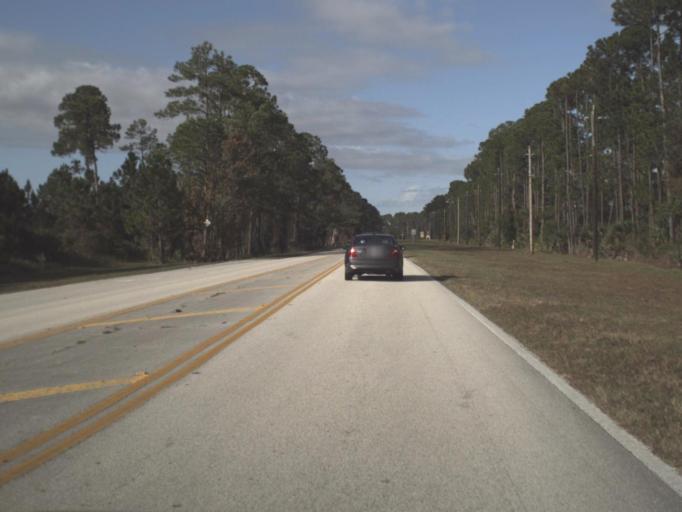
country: US
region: Florida
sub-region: Volusia County
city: Holly Hill
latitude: 29.2335
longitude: -81.0970
